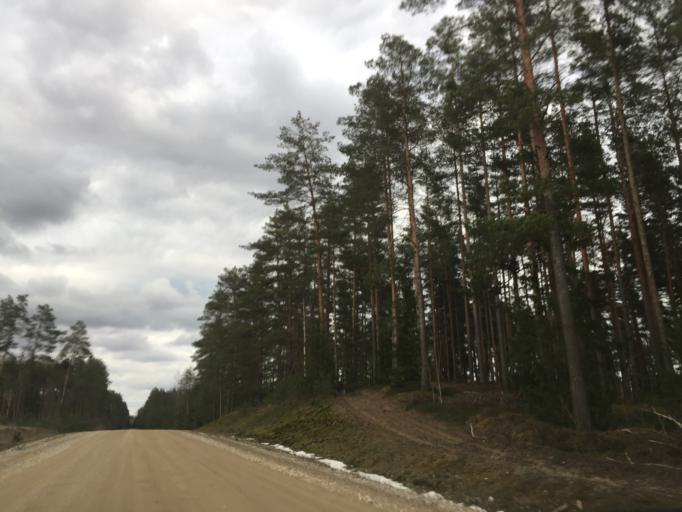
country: LV
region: Jaunjelgava
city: Jaunjelgava
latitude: 56.5856
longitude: 25.0340
